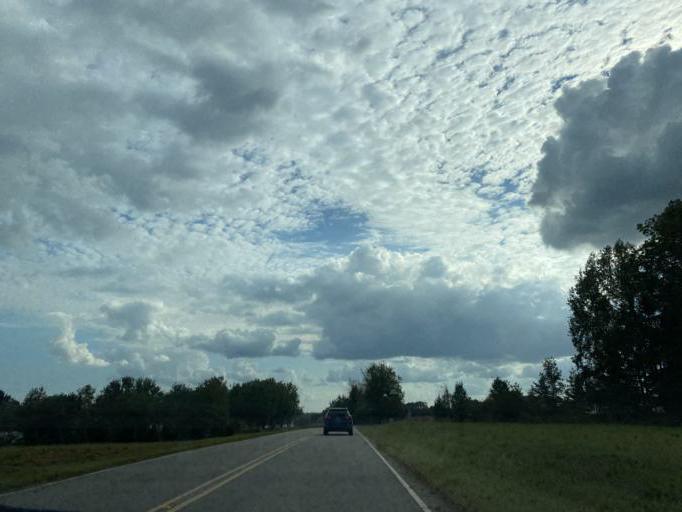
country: US
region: South Carolina
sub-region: Cherokee County
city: Gaffney
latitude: 35.0760
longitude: -81.7128
